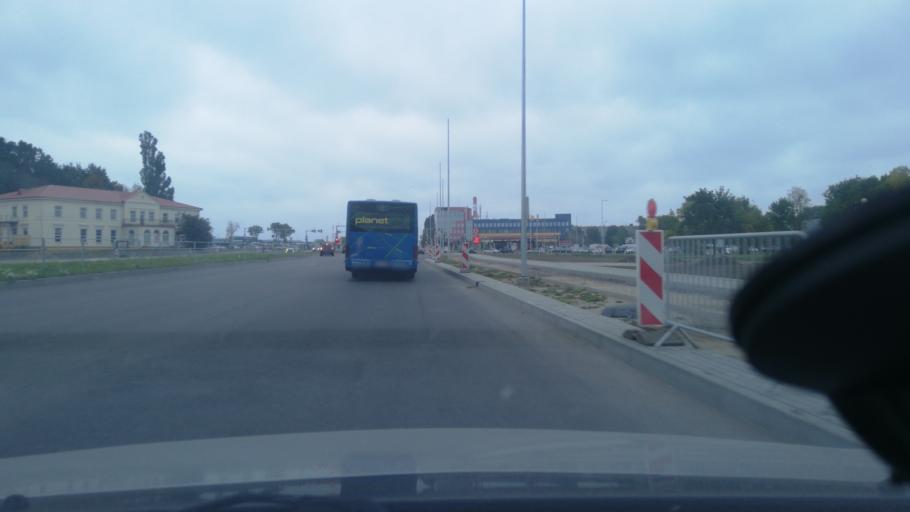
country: LT
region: Klaipedos apskritis
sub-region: Klaipeda
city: Klaipeda
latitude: 55.7064
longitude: 21.1586
